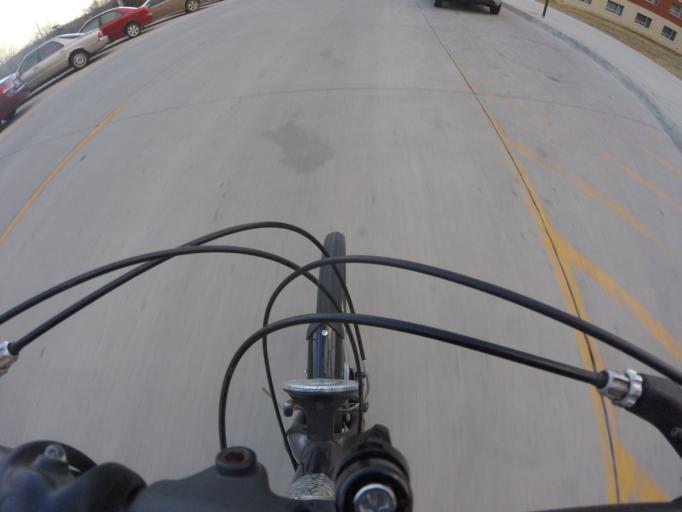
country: US
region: Kansas
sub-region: Douglas County
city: Lawrence
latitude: 38.9484
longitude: -95.2609
